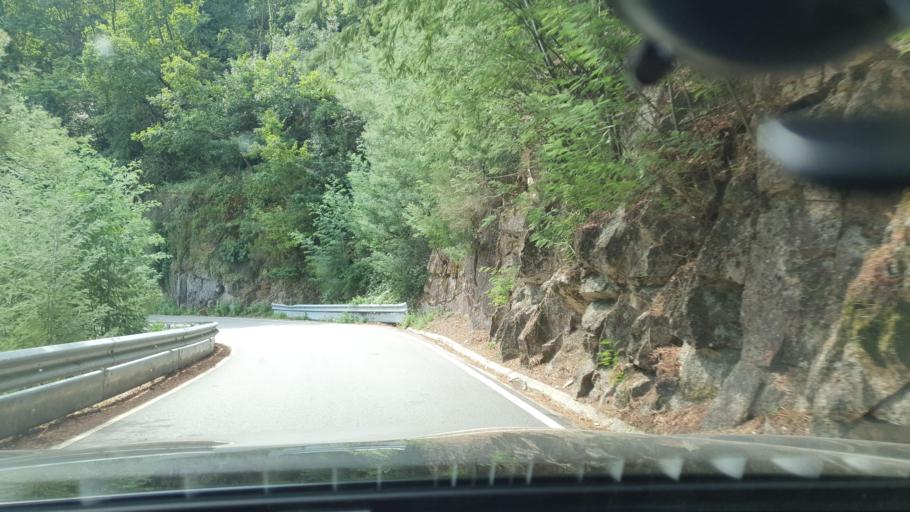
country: PT
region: Braga
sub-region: Vieira do Minho
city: Vieira do Minho
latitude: 41.6870
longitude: -8.0931
